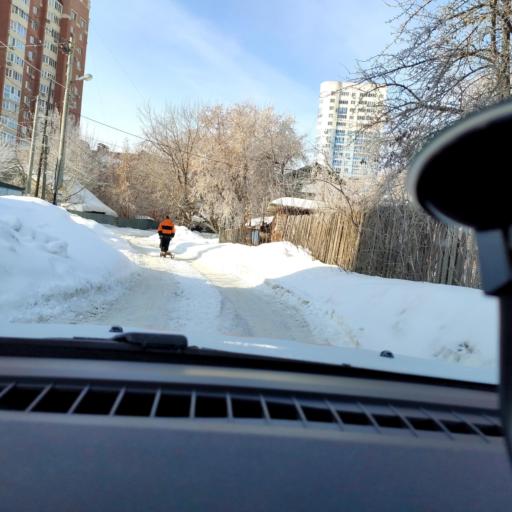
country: RU
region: Samara
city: Samara
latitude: 53.2251
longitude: 50.1547
